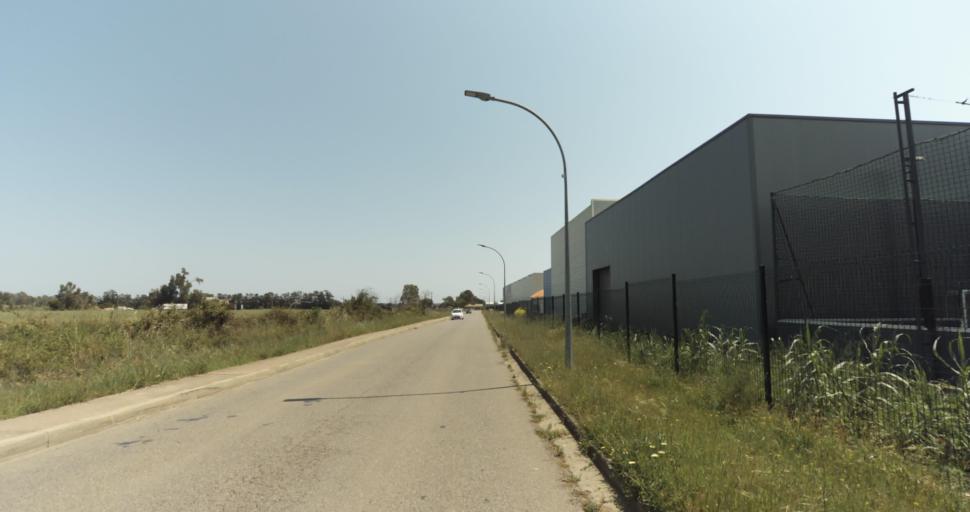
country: FR
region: Corsica
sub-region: Departement de la Haute-Corse
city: Biguglia
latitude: 42.6060
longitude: 9.4347
